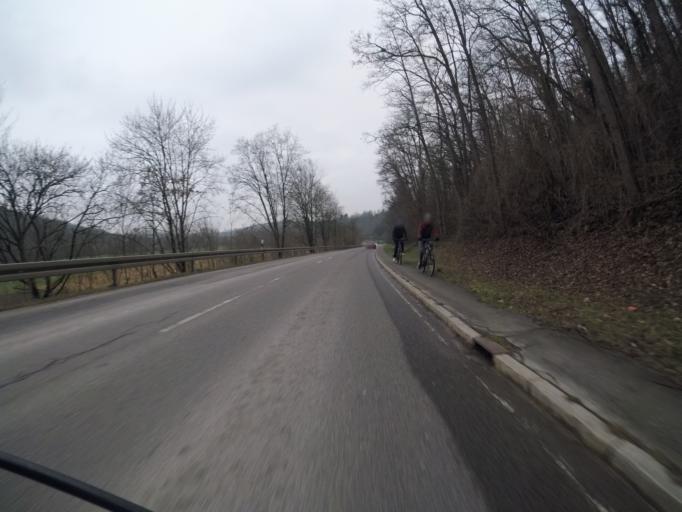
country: DE
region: Baden-Wuerttemberg
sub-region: Regierungsbezirk Stuttgart
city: Kirchberg an der Murr
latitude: 48.9445
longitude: 9.3235
